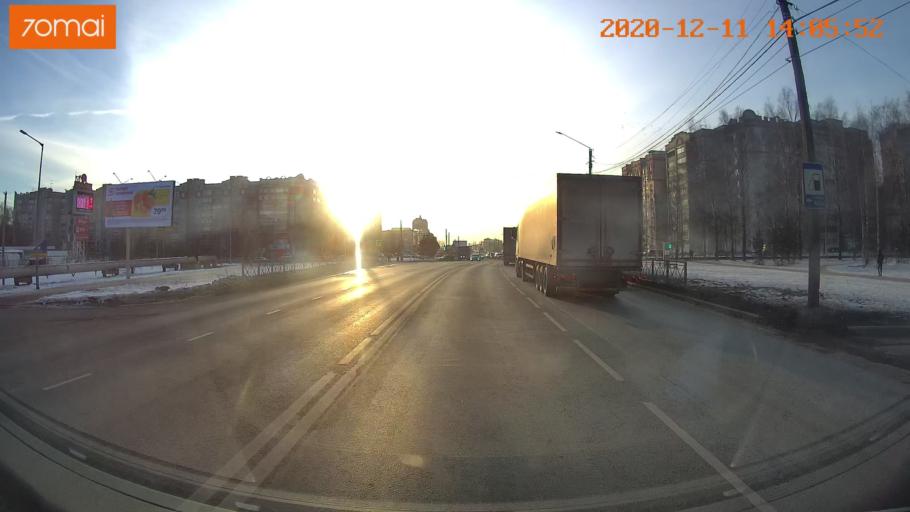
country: RU
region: Kostroma
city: Oktyabr'skiy
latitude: 57.7453
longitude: 41.0093
